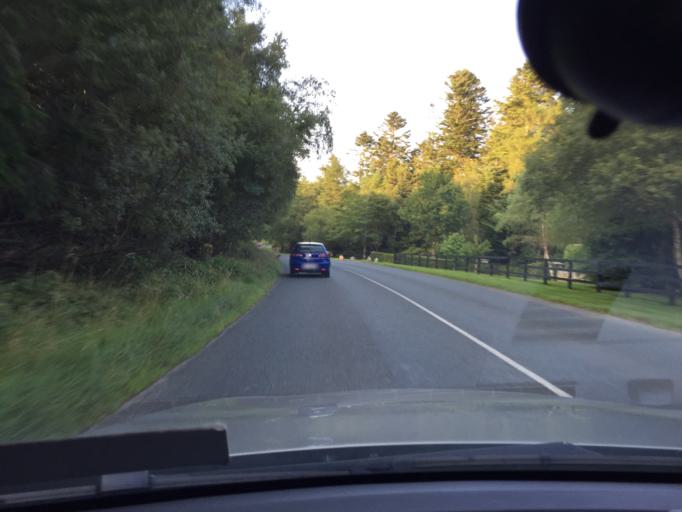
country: IE
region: Leinster
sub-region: Wicklow
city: Rathdrum
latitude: 53.0244
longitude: -6.2688
